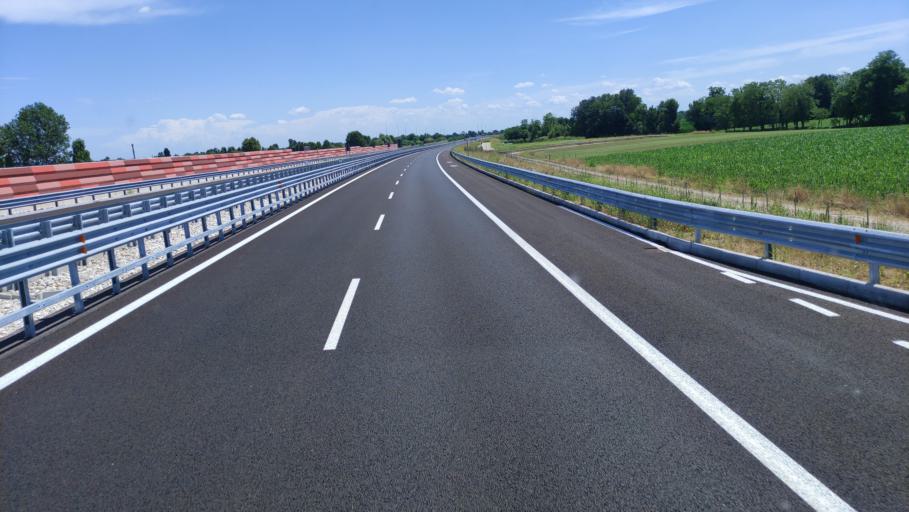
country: IT
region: Veneto
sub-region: Provincia di Treviso
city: Villa d'Asolo
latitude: 45.7545
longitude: 11.8868
